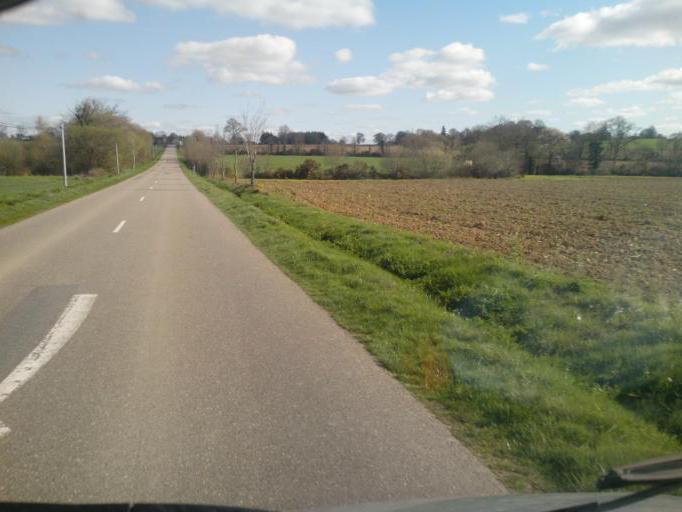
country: FR
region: Brittany
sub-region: Departement d'Ille-et-Vilaine
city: Maxent
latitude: 47.9725
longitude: -2.0209
